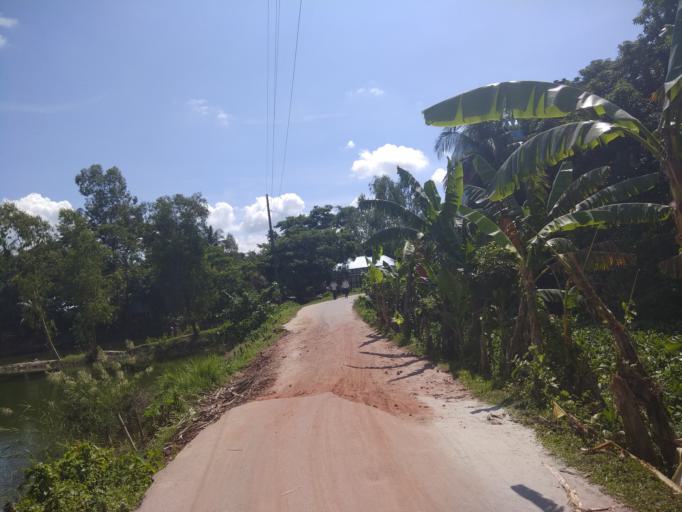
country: BD
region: Dhaka
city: Narayanganj
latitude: 23.4462
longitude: 90.4800
